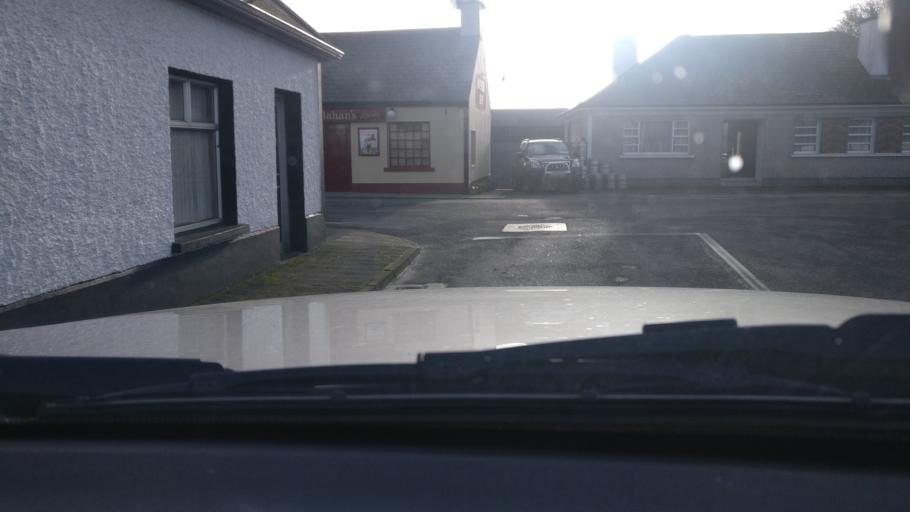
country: IE
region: Connaught
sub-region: County Galway
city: Ballinasloe
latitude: 53.2359
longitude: -8.2720
